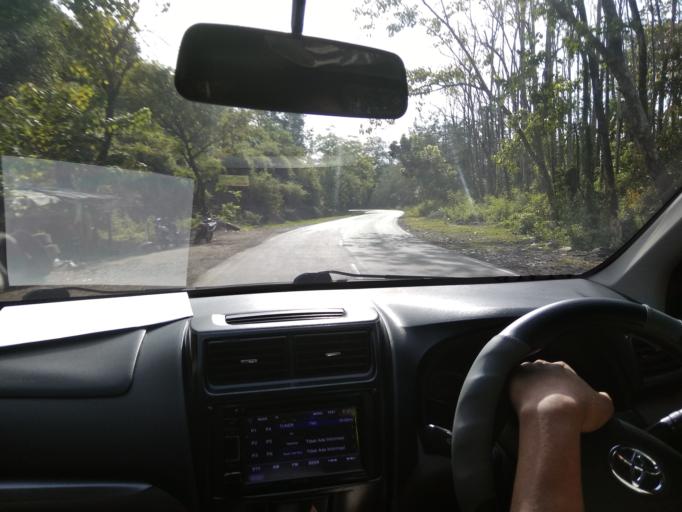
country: ID
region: South Sulawesi
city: Makassar
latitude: -5.2606
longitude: 119.5805
